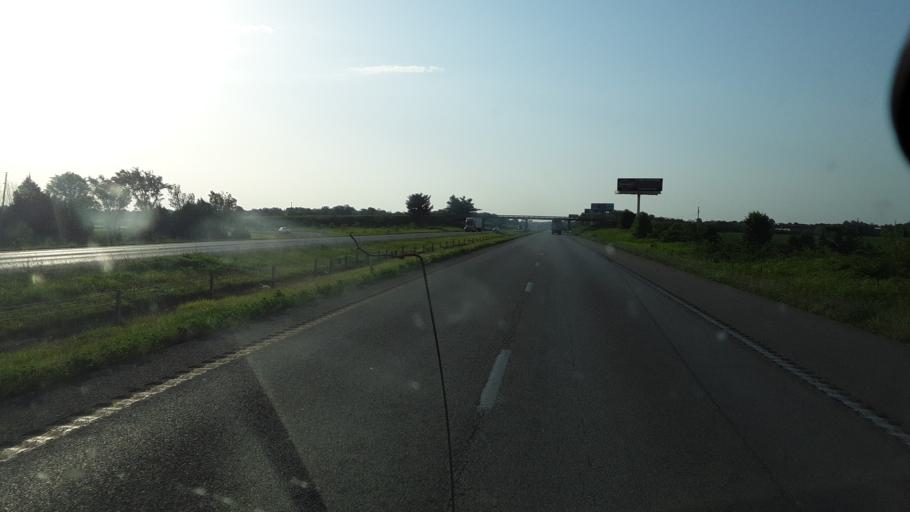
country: US
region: Missouri
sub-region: Gasconade County
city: Hermann
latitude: 38.8662
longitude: -91.3341
